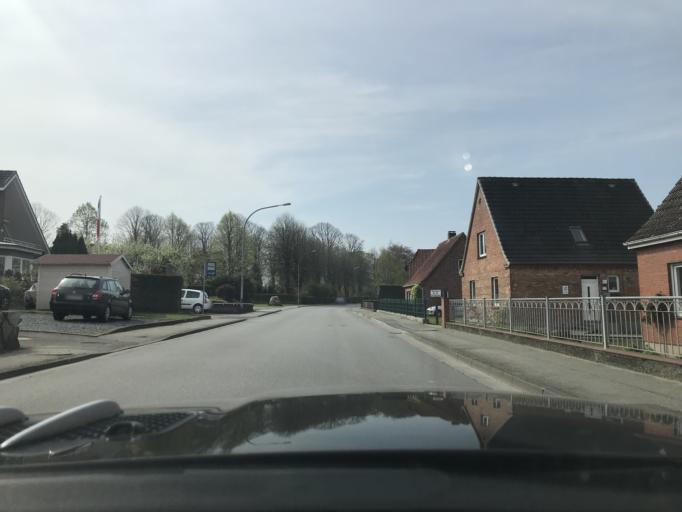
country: DE
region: Schleswig-Holstein
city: Grube
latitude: 54.2287
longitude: 11.0359
